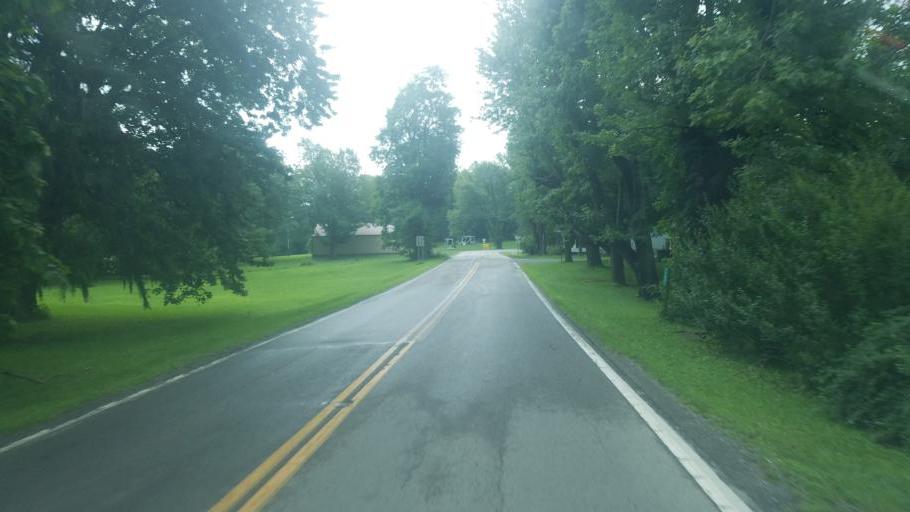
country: US
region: Ohio
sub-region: Logan County
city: Russells Point
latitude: 40.5612
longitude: -83.8351
